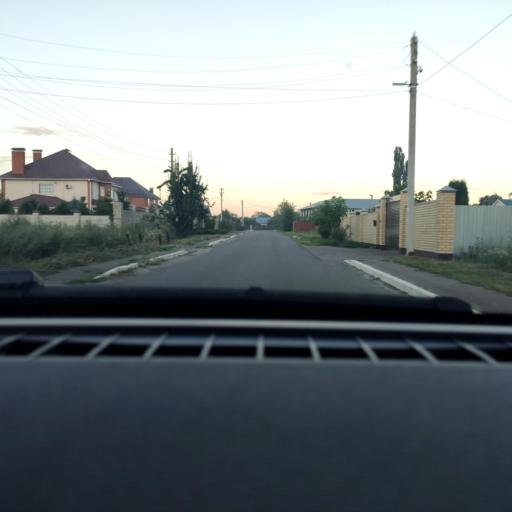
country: RU
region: Voronezj
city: Novaya Usman'
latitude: 51.6561
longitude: 39.3328
